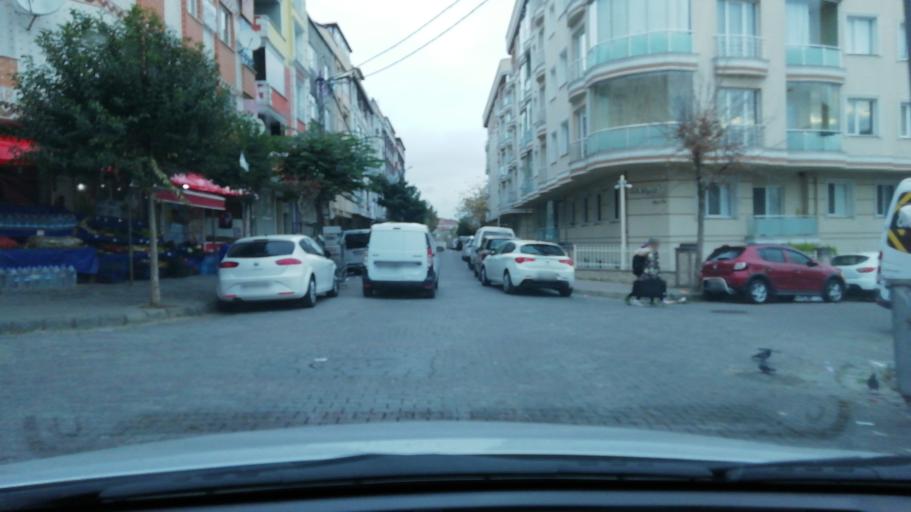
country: TR
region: Istanbul
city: Bagcilar
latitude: 41.0203
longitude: 28.8310
